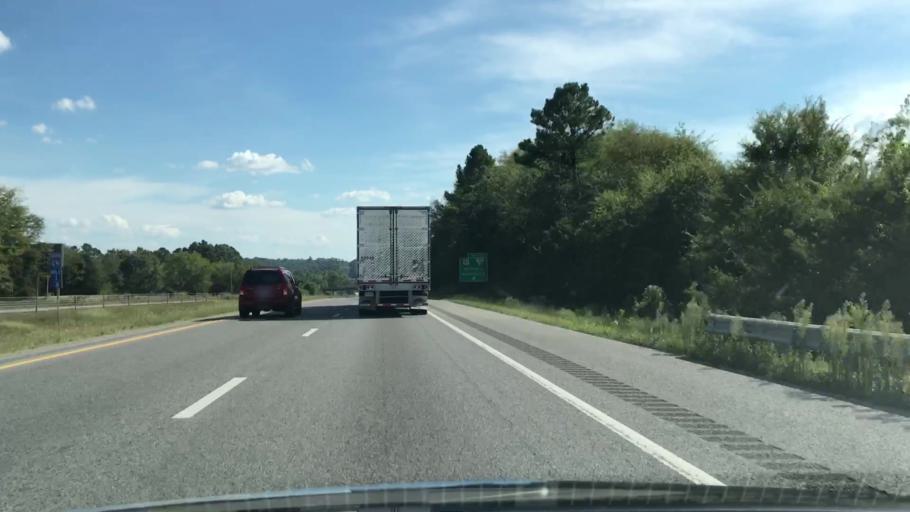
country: US
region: Alabama
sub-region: Limestone County
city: Ardmore
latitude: 35.0189
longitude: -86.8794
